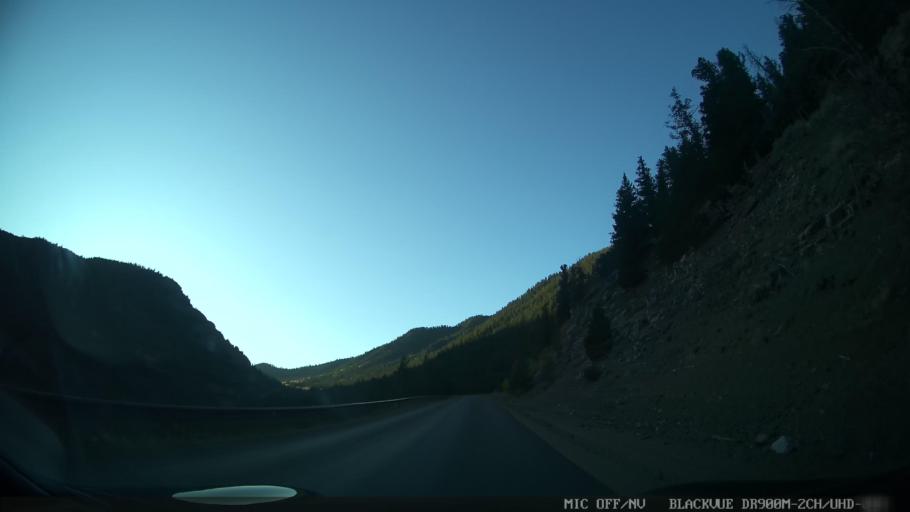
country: US
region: Colorado
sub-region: Grand County
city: Kremmling
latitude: 40.0010
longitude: -106.4842
